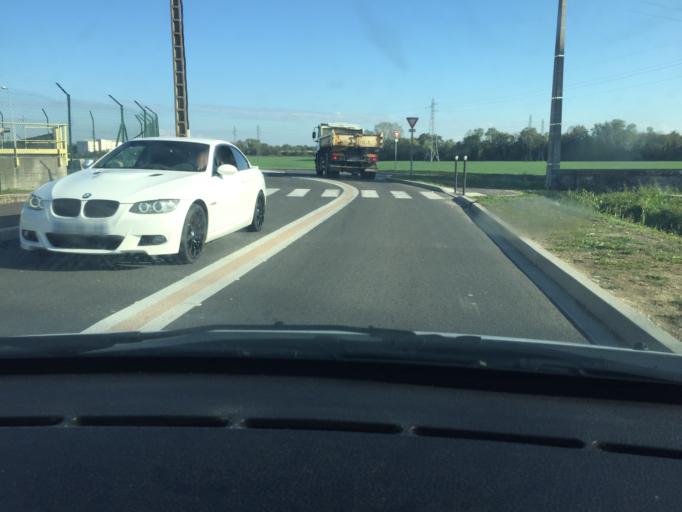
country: FR
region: Rhone-Alpes
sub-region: Departement de l'Ain
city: Saint-Maurice-de-Beynost
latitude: 45.8216
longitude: 4.9786
